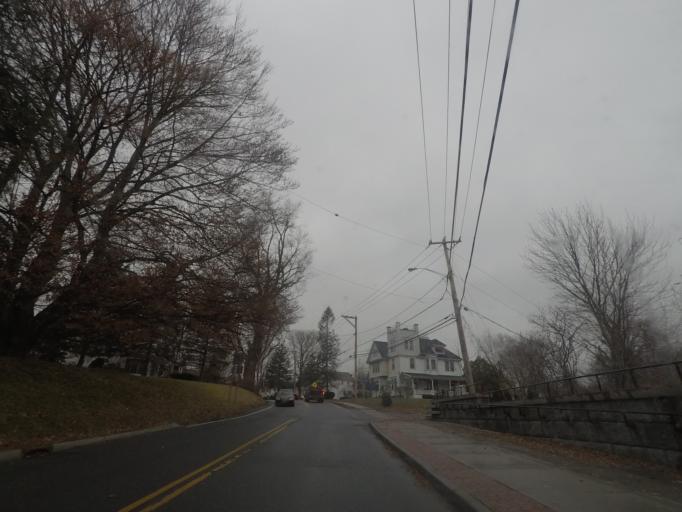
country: US
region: New York
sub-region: Saratoga County
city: Mechanicville
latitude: 42.9007
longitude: -73.6954
